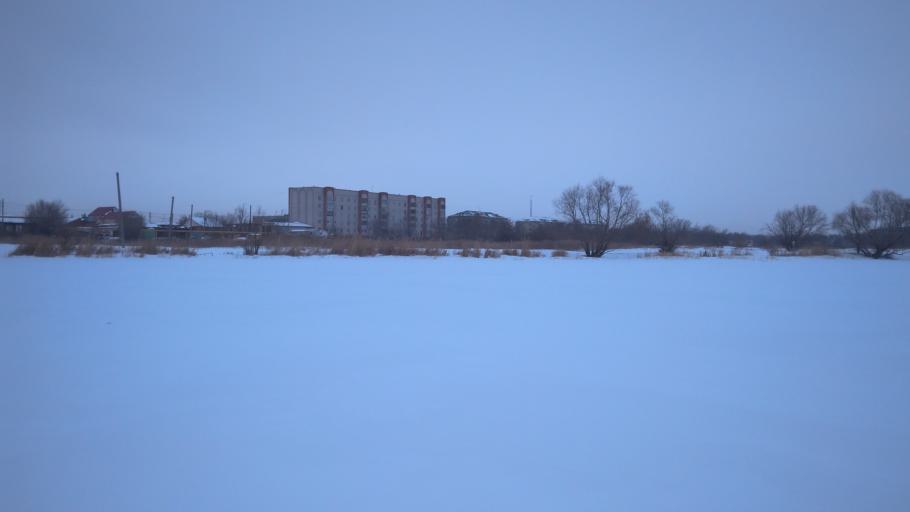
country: RU
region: Chelyabinsk
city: Troitsk
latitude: 54.0815
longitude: 61.5726
